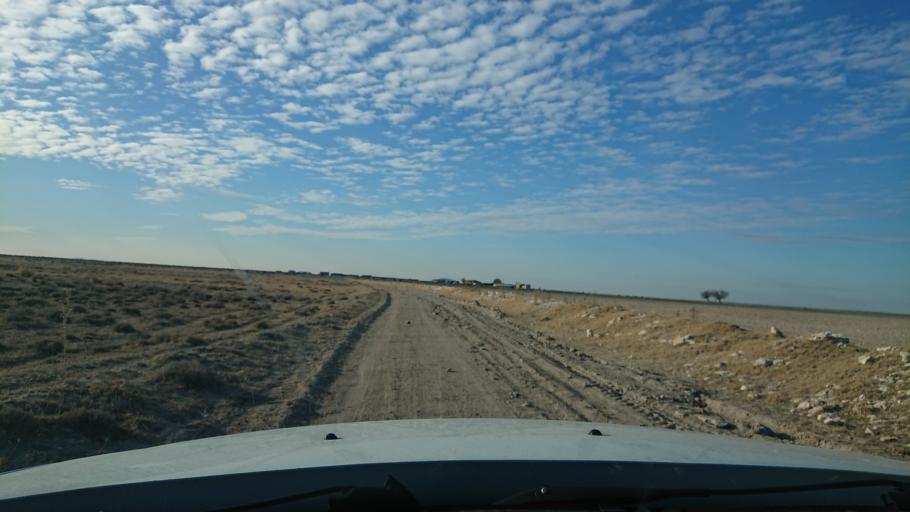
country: TR
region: Aksaray
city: Eskil
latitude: 38.5653
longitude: 33.3019
